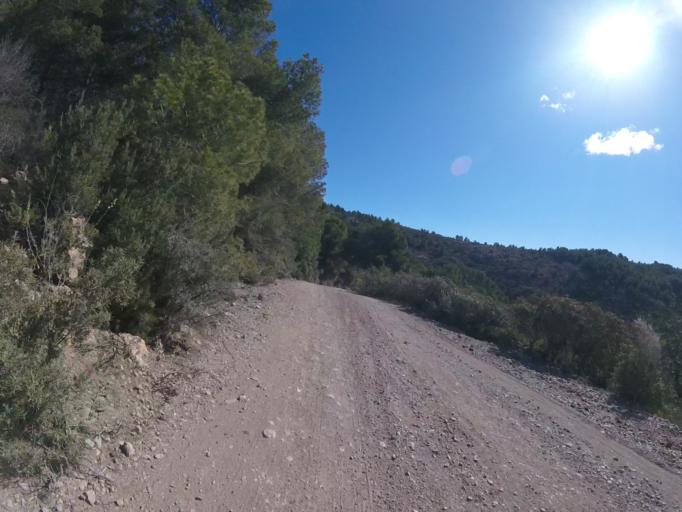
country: ES
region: Valencia
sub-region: Provincia de Castello
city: Benicassim
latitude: 40.0735
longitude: 0.0768
